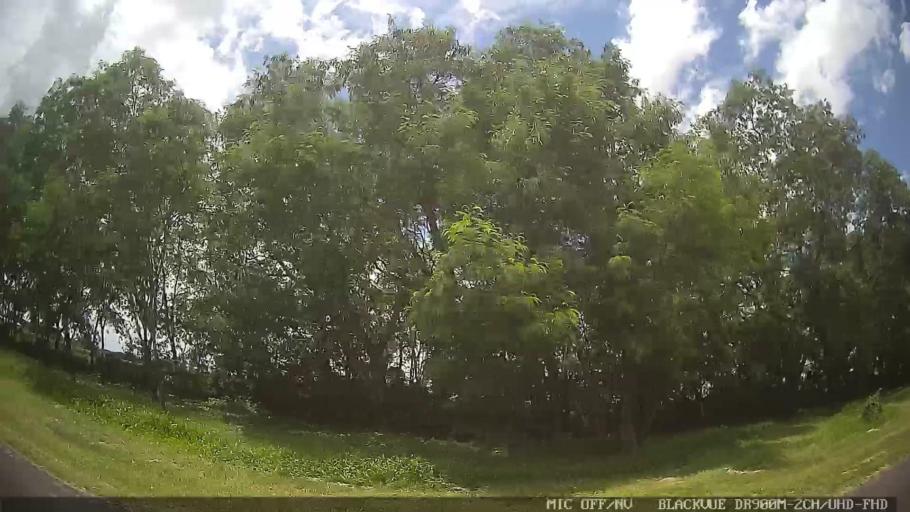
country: BR
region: Sao Paulo
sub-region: Laranjal Paulista
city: Laranjal Paulista
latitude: -23.0381
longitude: -47.8598
